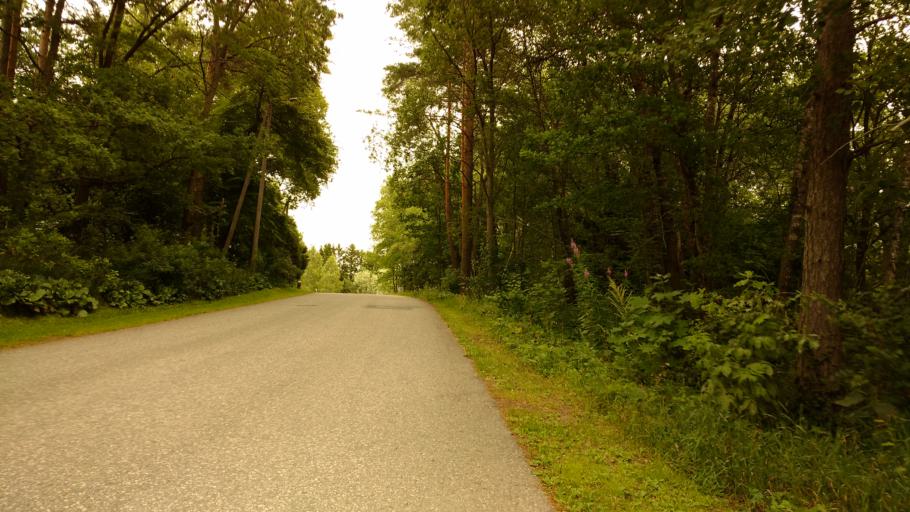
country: FI
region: Varsinais-Suomi
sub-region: Turku
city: Kaarina
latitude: 60.4391
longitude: 22.3534
